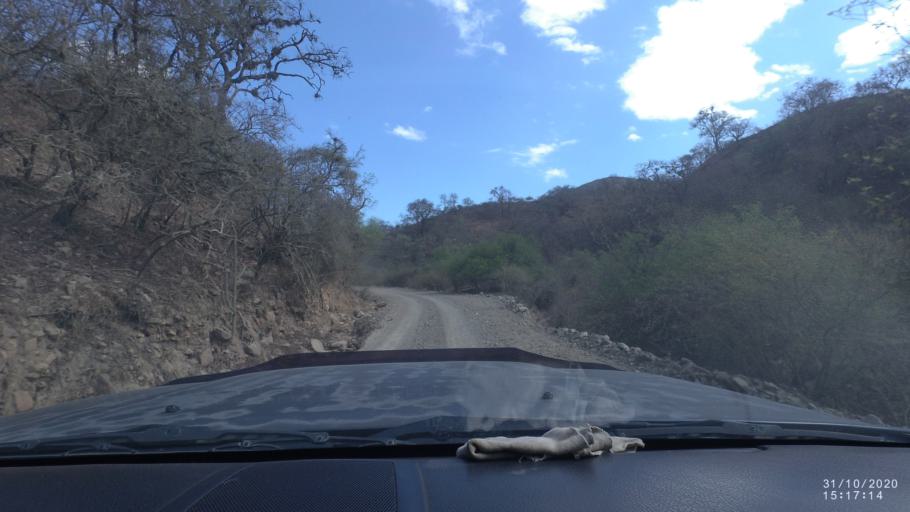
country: BO
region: Cochabamba
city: Aiquile
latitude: -18.3388
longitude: -64.7685
